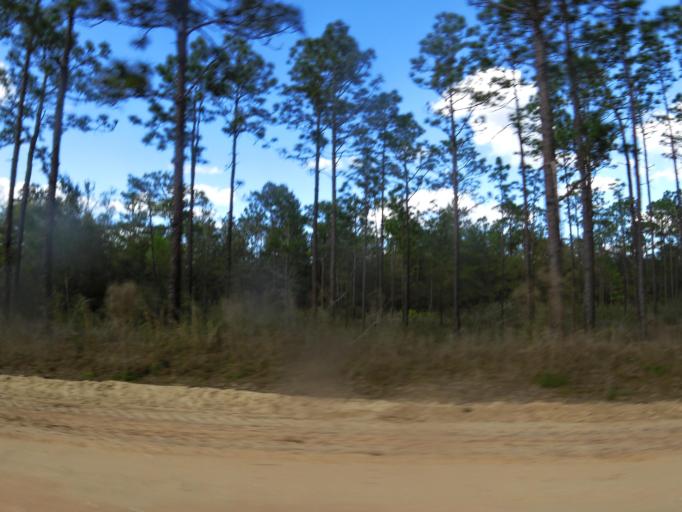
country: US
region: Florida
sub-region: Clay County
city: Keystone Heights
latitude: 29.7876
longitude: -81.8741
